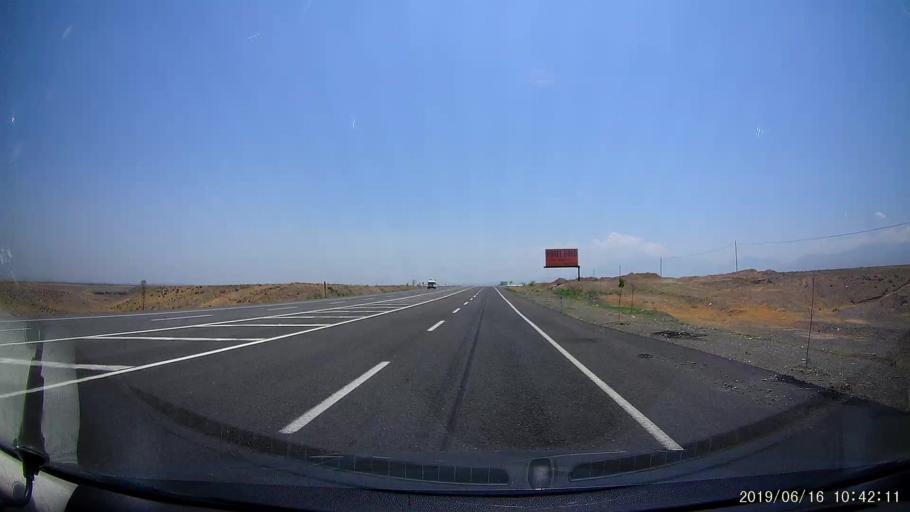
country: AM
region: Armavir
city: Shenavan
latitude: 40.0438
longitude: 43.8012
